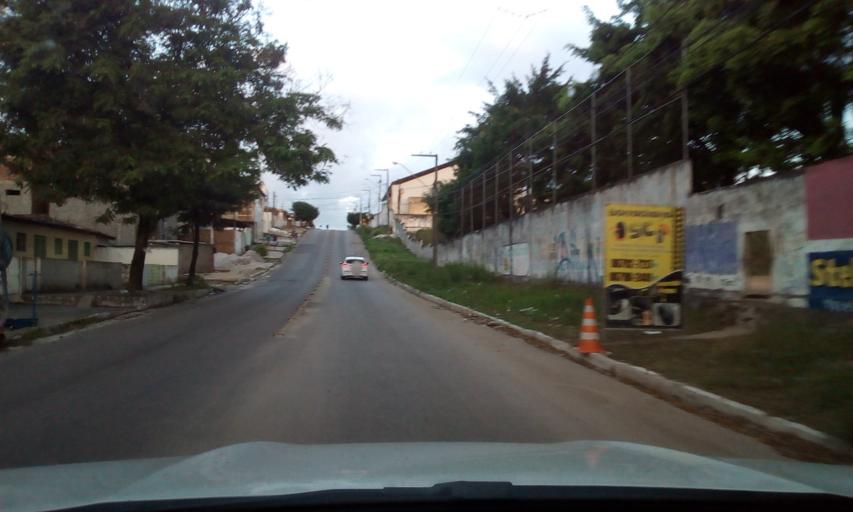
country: BR
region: Paraiba
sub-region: Joao Pessoa
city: Joao Pessoa
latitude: -7.1769
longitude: -34.8826
